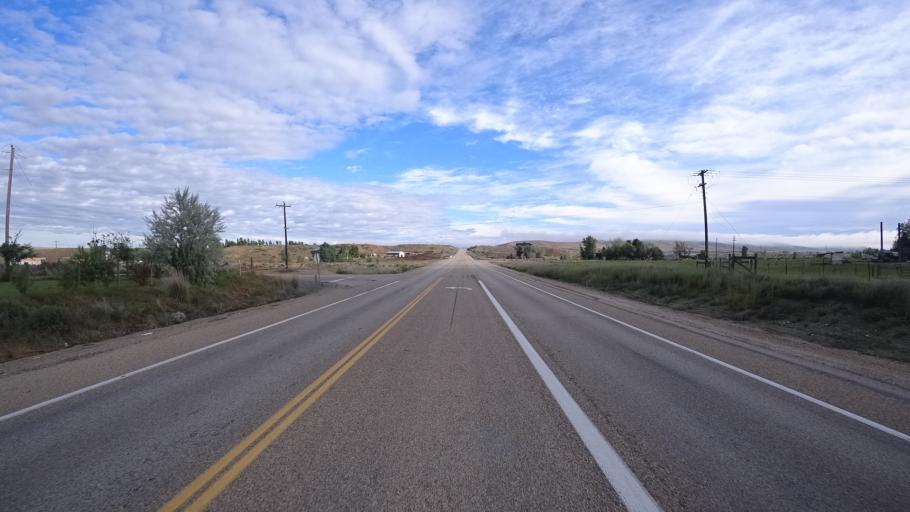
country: US
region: Idaho
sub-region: Ada County
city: Star
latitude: 43.7787
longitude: -116.4725
